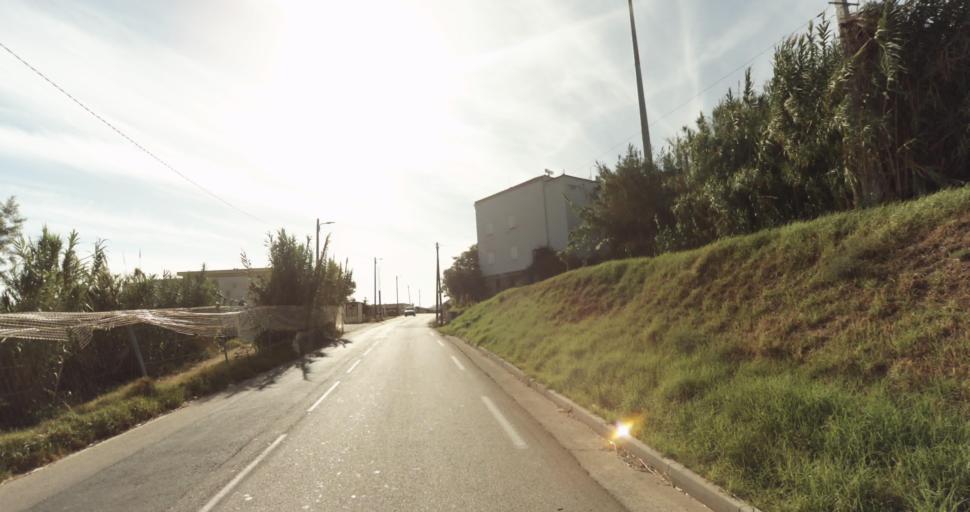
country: FR
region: Corsica
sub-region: Departement de la Corse-du-Sud
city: Ajaccio
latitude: 41.9303
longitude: 8.7781
